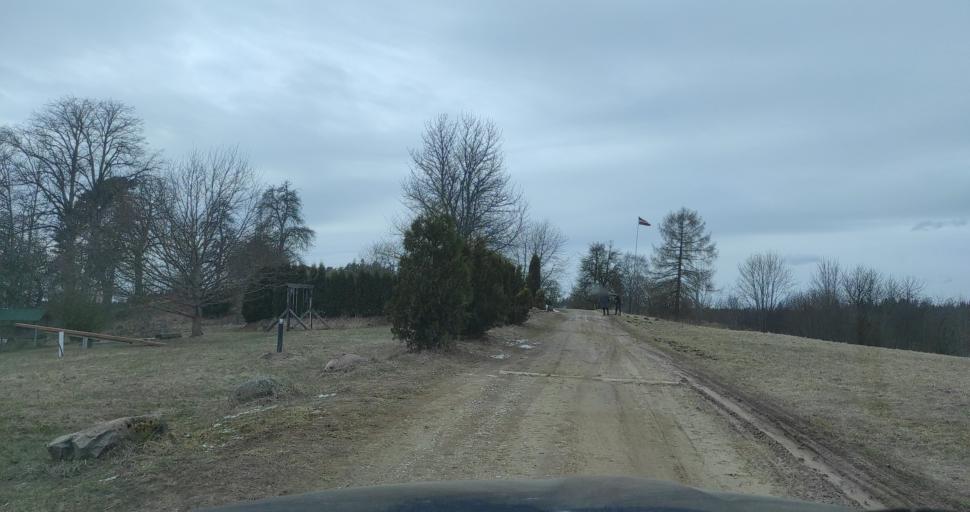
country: LV
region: Tukuma Rajons
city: Tukums
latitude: 57.0986
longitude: 23.0889
